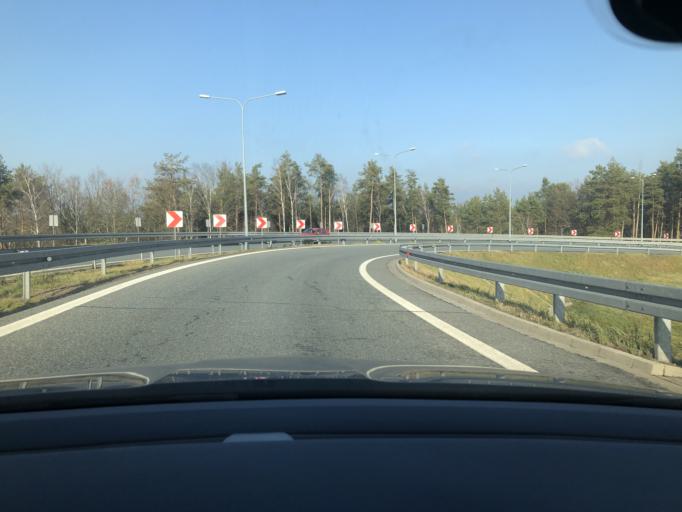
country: PL
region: Lubusz
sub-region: Powiat swiebodzinski
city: Swiebodzin
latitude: 52.3242
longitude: 15.5473
